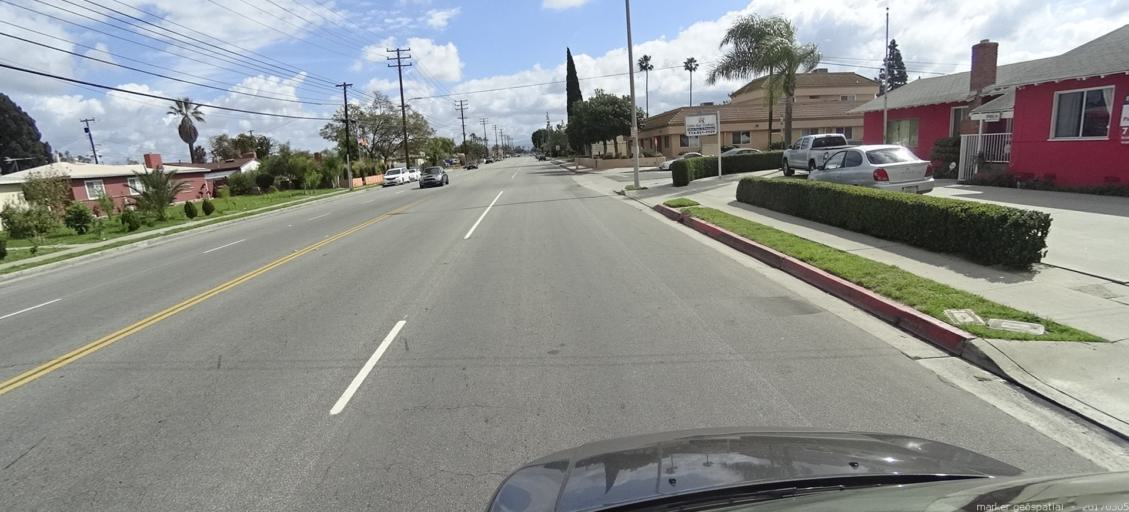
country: US
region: California
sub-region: Orange County
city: Stanton
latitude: 33.8103
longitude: -117.9800
